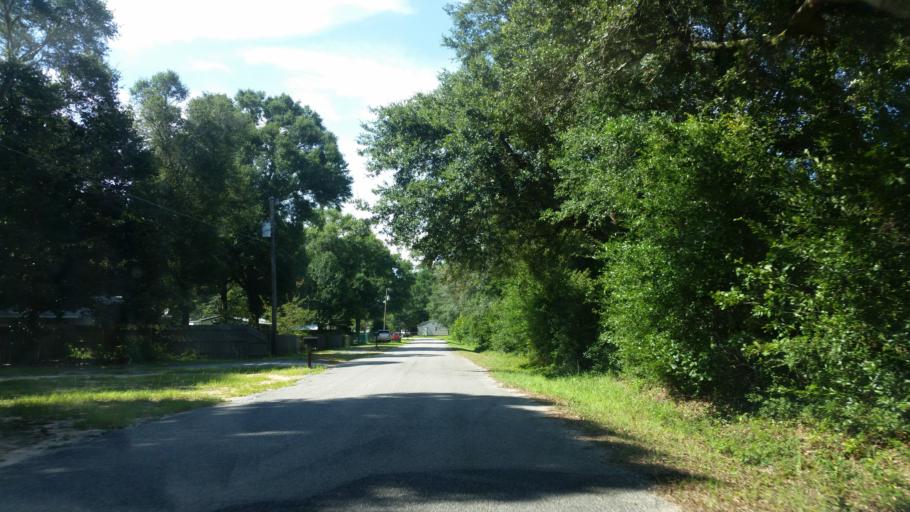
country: US
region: Florida
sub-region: Santa Rosa County
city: Pace
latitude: 30.5940
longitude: -87.1449
